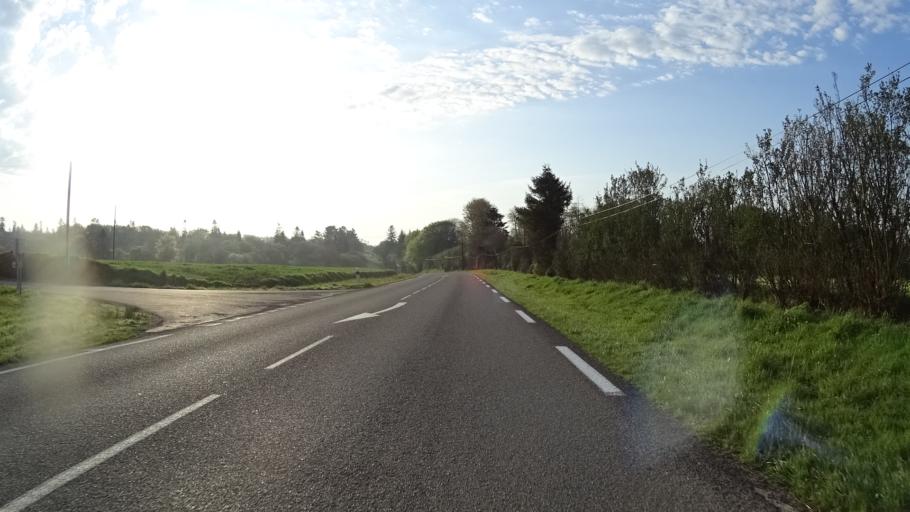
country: FR
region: Brittany
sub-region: Departement du Finistere
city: La Roche-Maurice
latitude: 48.4378
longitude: -4.1716
